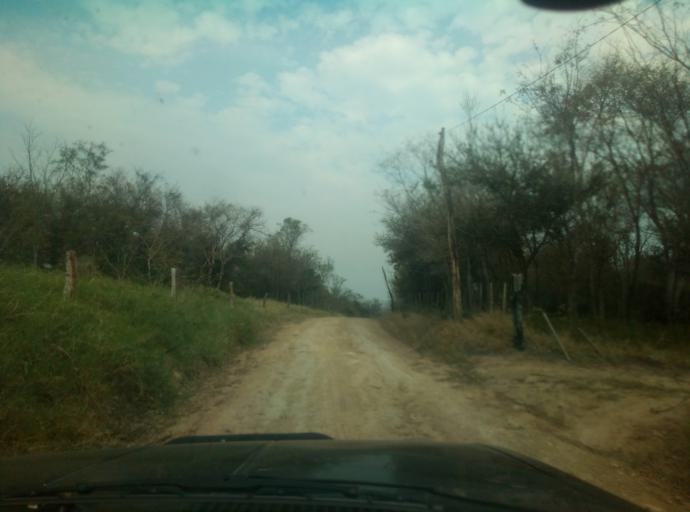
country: PY
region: Caaguazu
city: San Joaquin
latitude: -25.0935
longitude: -56.1410
